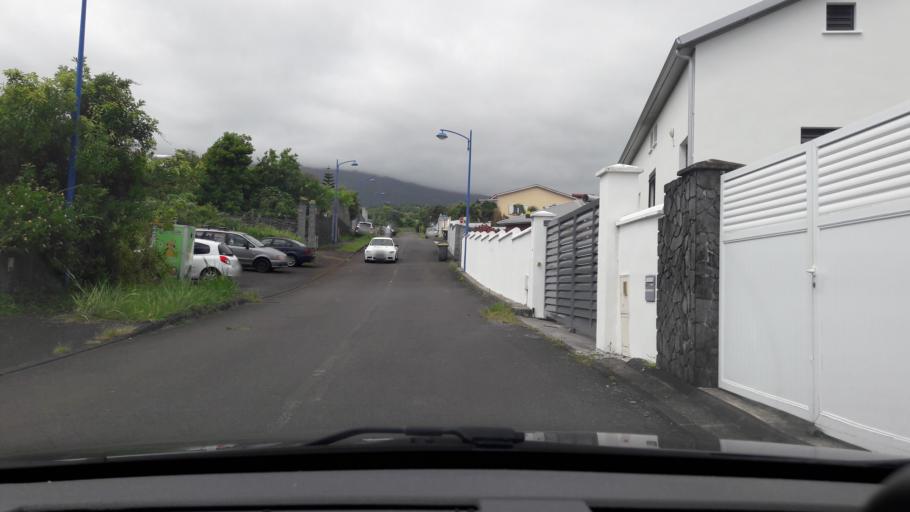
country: RE
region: Reunion
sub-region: Reunion
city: Saint-Benoit
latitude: -21.0935
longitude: 55.7031
